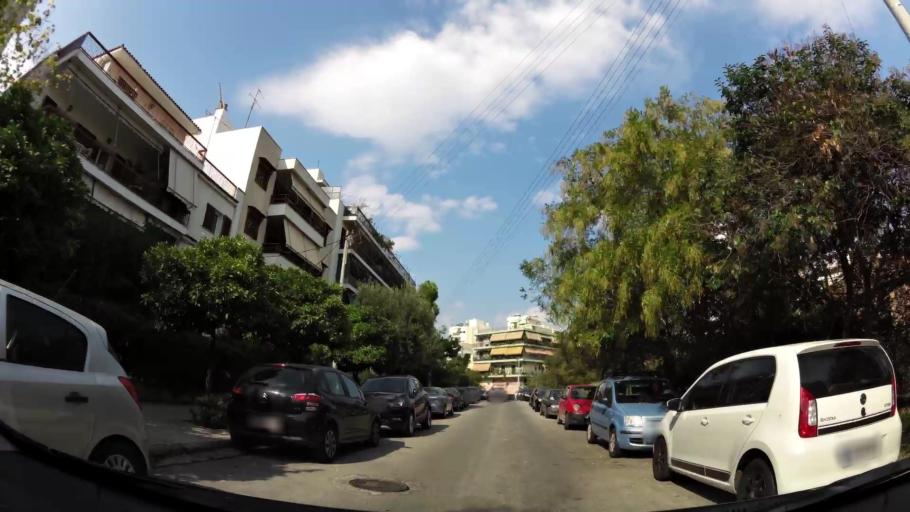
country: GR
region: Attica
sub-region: Nomarchia Athinas
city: Galatsi
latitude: 38.0215
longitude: 23.7417
